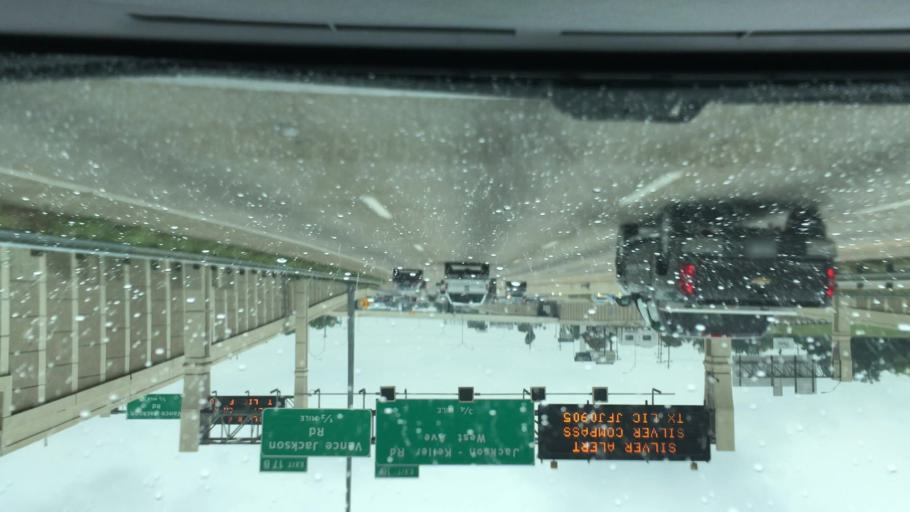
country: US
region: Texas
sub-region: Bexar County
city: Balcones Heights
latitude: 29.5051
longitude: -98.5459
